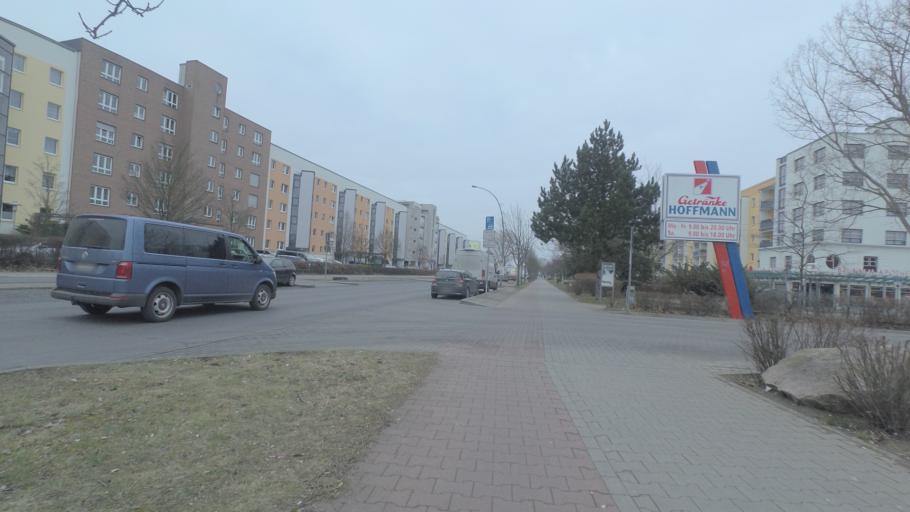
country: DE
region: Brandenburg
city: Ludwigsfelde
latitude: 52.3087
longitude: 13.2465
